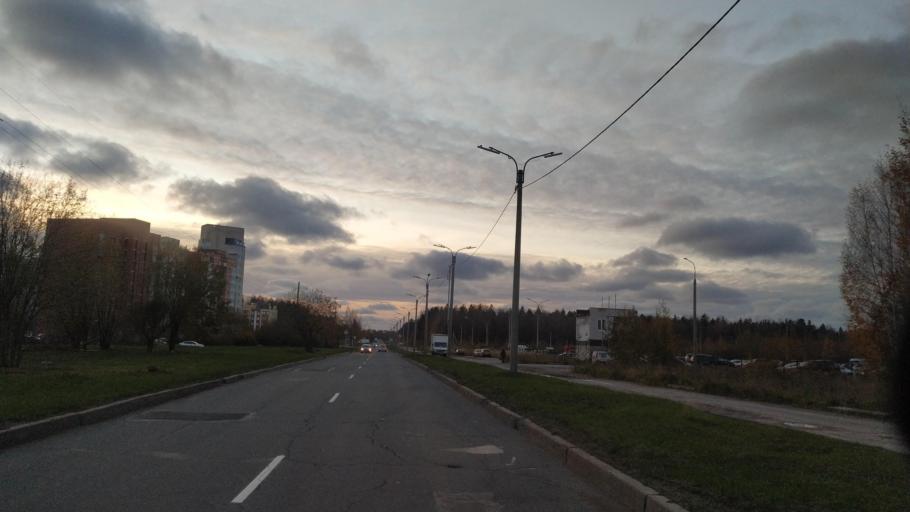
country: RU
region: Leningrad
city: Sosnovyy Bor
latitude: 59.9180
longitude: 29.0894
